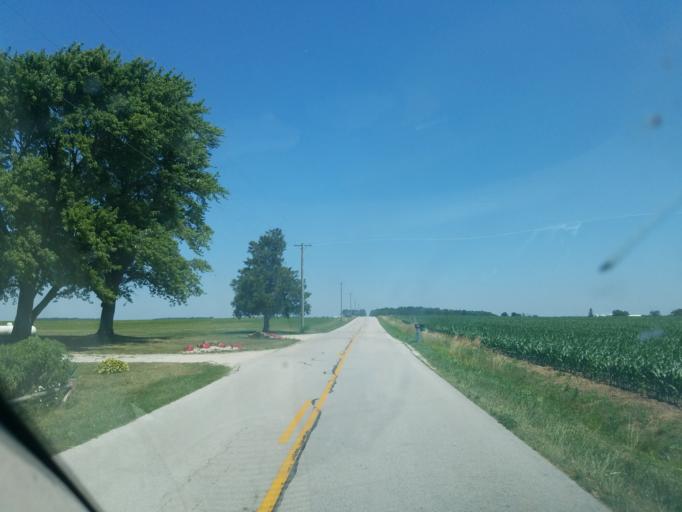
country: US
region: Ohio
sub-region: Mercer County
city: Rockford
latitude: 40.6636
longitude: -84.7086
